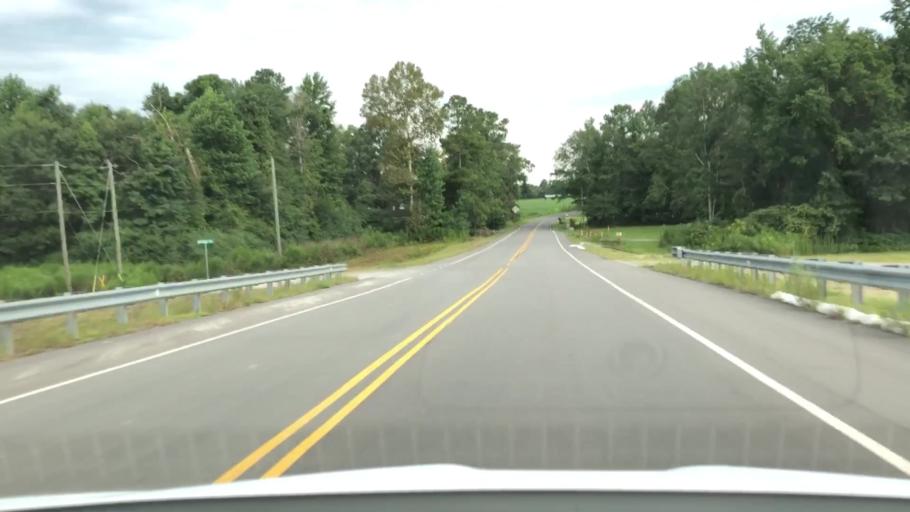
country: US
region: North Carolina
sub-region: Jones County
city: Maysville
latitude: 34.9125
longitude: -77.2392
